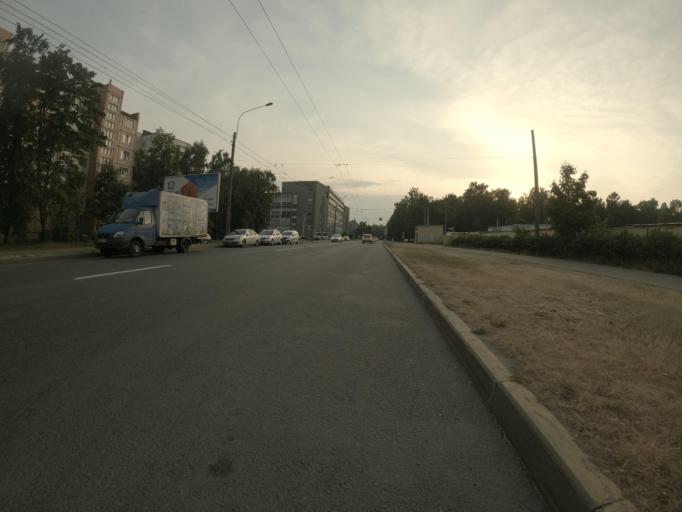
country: RU
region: Leningrad
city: Kalininskiy
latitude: 59.9866
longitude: 30.4036
